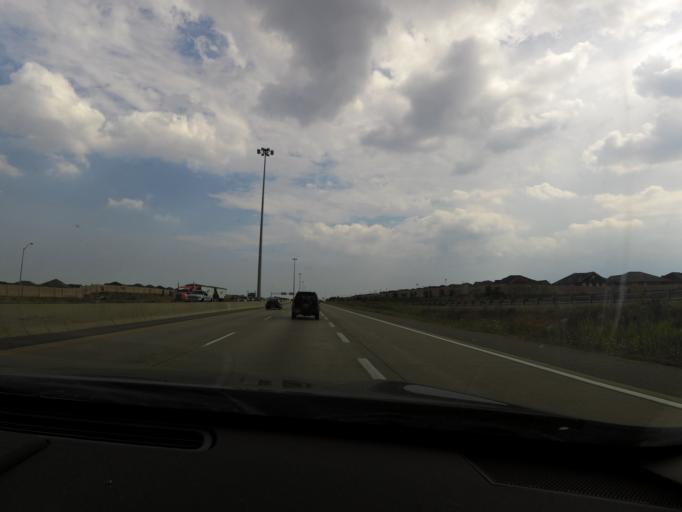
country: CA
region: Ontario
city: Brampton
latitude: 43.7372
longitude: -79.7770
